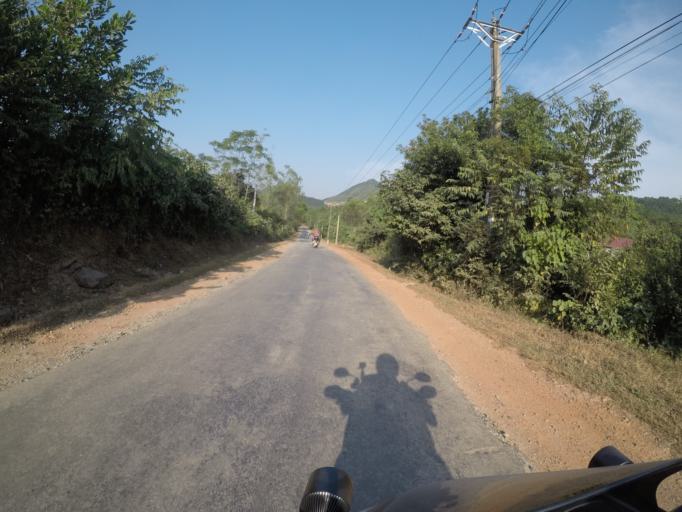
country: VN
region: Vinh Phuc
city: Huong Canh
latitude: 21.3584
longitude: 105.7125
